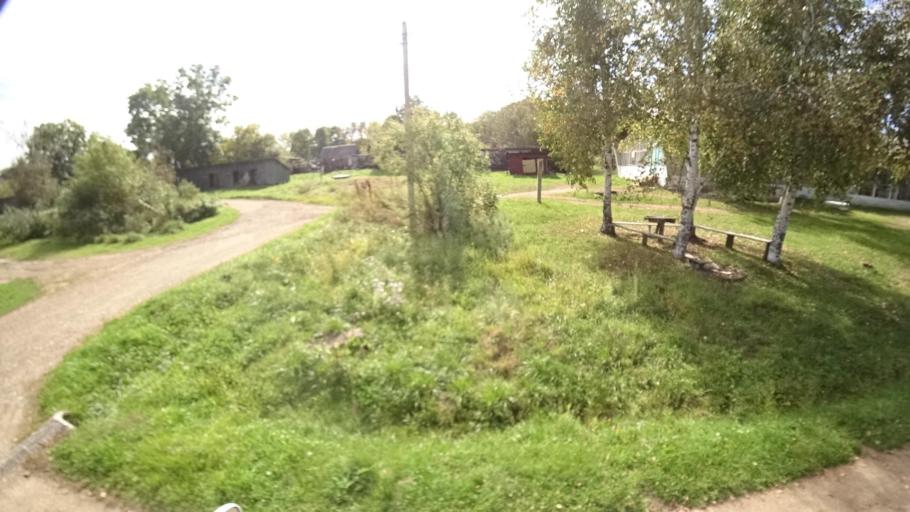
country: RU
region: Primorskiy
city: Yakovlevka
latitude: 44.4002
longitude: 133.6001
